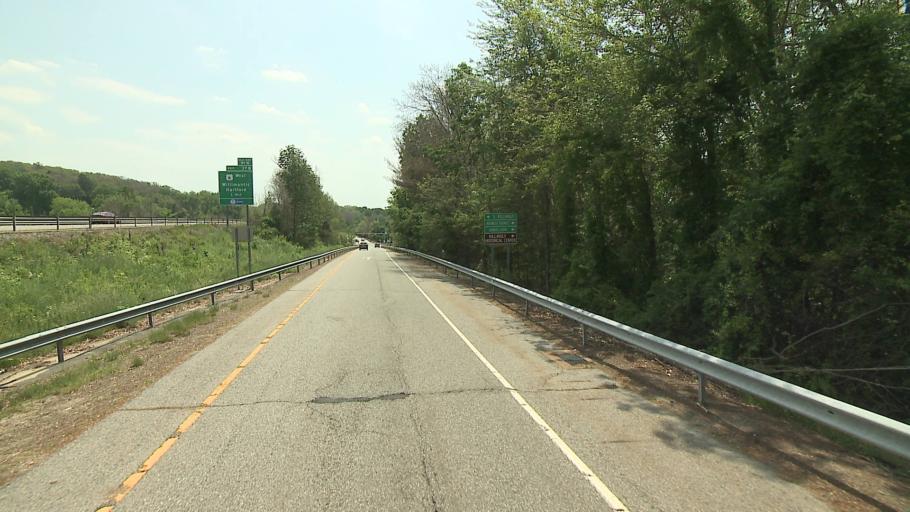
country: US
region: Connecticut
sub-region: Windham County
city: Danielson
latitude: 41.8112
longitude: -71.8719
